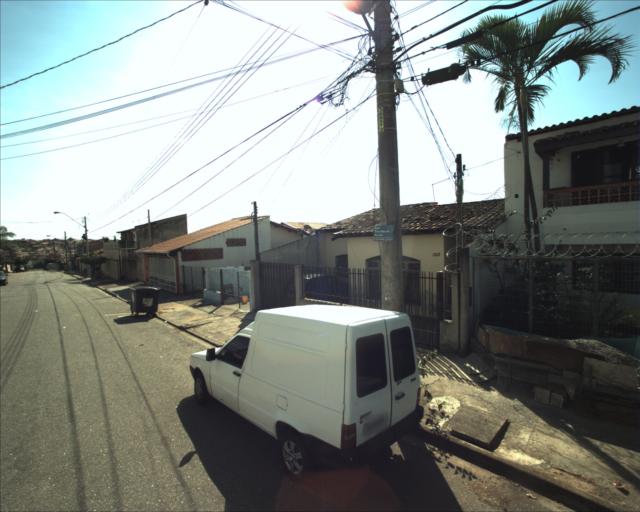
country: BR
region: Sao Paulo
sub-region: Sorocaba
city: Sorocaba
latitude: -23.4991
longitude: -47.5171
